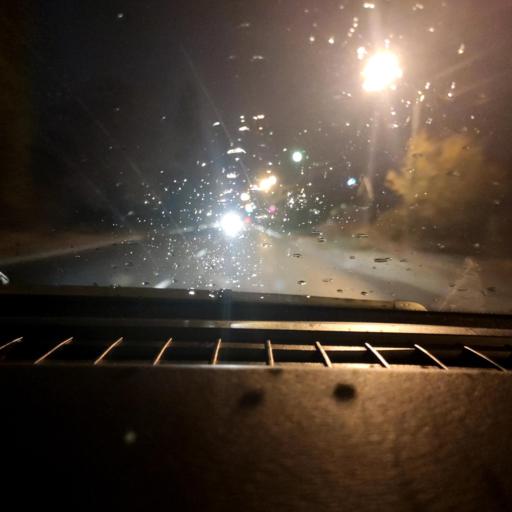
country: RU
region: Voronezj
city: Maslovka
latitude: 51.6203
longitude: 39.2514
